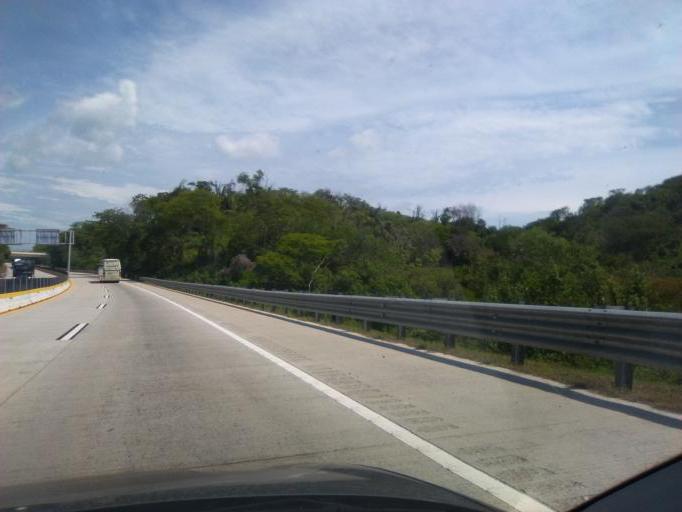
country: MX
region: Guerrero
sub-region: Acapulco de Juarez
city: Colonia Nueva Revolucion
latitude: 16.9294
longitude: -99.7920
